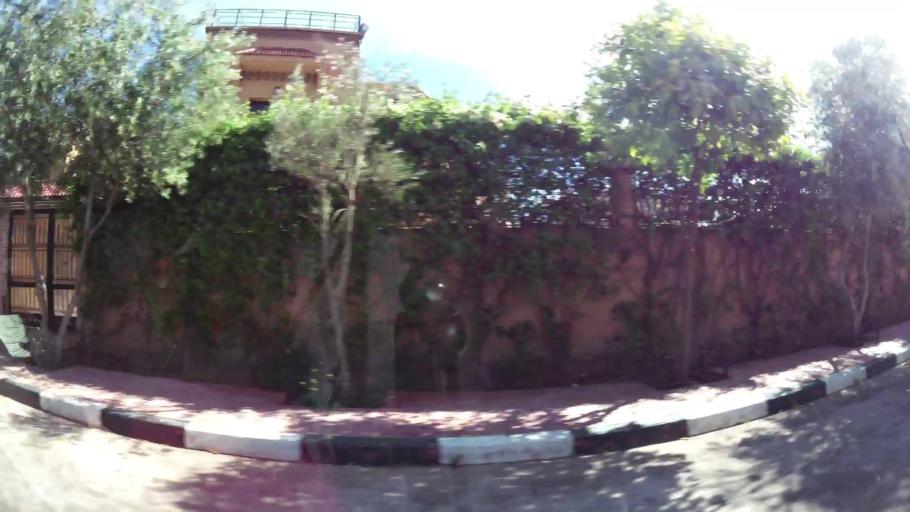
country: MA
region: Marrakech-Tensift-Al Haouz
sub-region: Marrakech
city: Marrakesh
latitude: 31.6560
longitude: -8.0585
